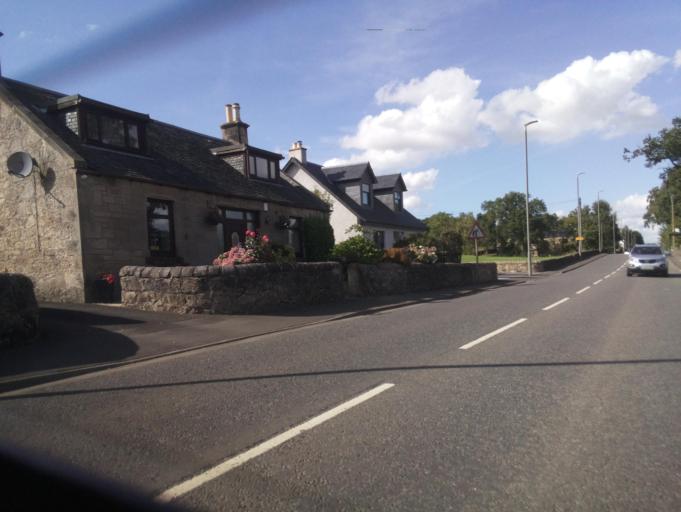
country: GB
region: Scotland
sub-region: Stirling
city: Cowie
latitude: 56.0583
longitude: -3.8695
